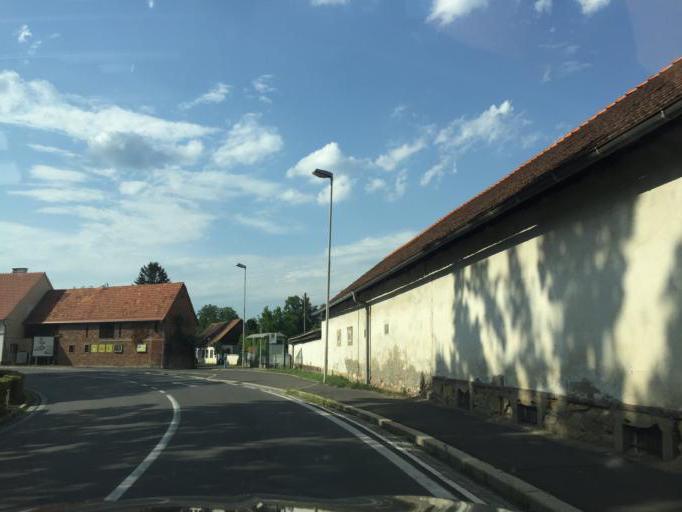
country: AT
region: Styria
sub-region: Politischer Bezirk Suedoststeiermark
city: Bad Radkersburg
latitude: 46.6902
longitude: 15.9900
